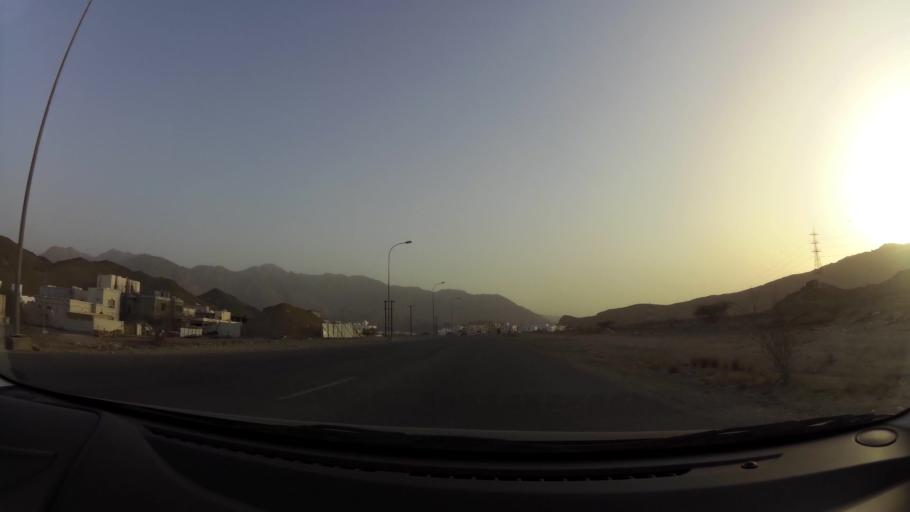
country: OM
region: Muhafazat Masqat
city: Bawshar
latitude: 23.4895
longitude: 58.3161
